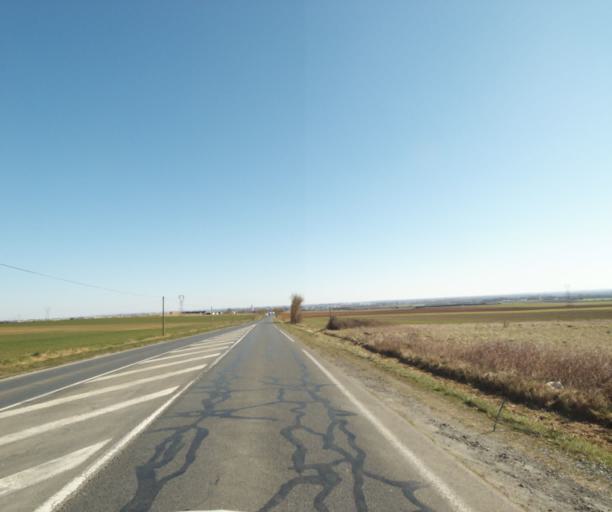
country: FR
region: Poitou-Charentes
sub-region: Departement des Deux-Sevres
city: Magne
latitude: 46.3528
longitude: -0.5238
